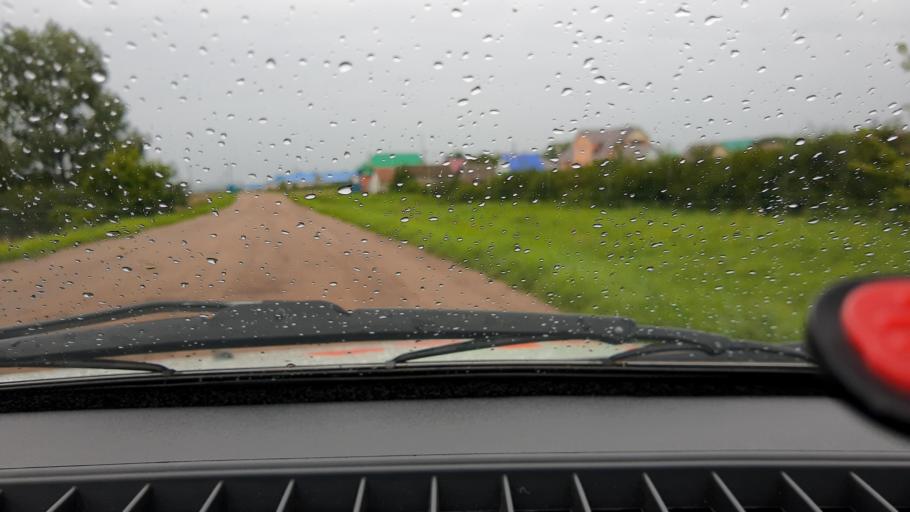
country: RU
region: Bashkortostan
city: Karmaskaly
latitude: 54.3822
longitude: 56.1132
